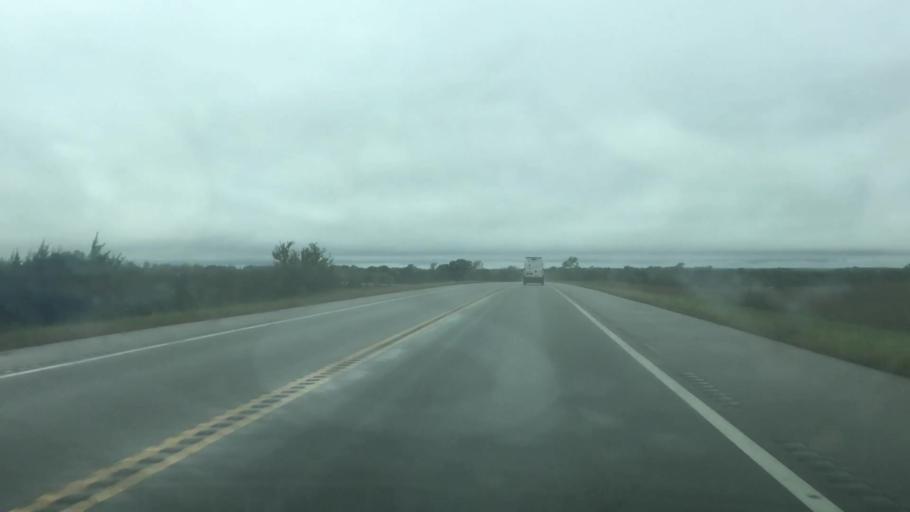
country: US
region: Kansas
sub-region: Anderson County
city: Garnett
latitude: 38.1633
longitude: -95.3013
